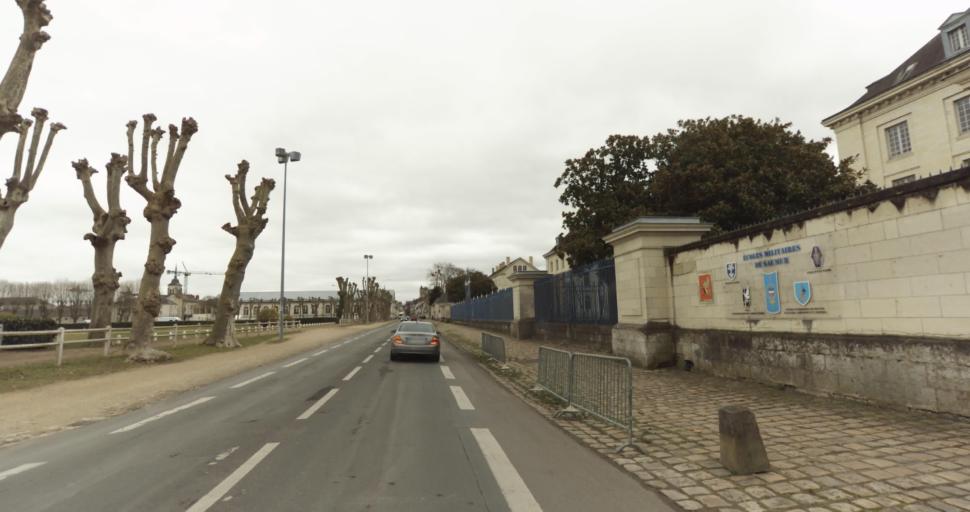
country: FR
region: Pays de la Loire
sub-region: Departement de Maine-et-Loire
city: Saumur
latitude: 47.2618
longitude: -0.0861
